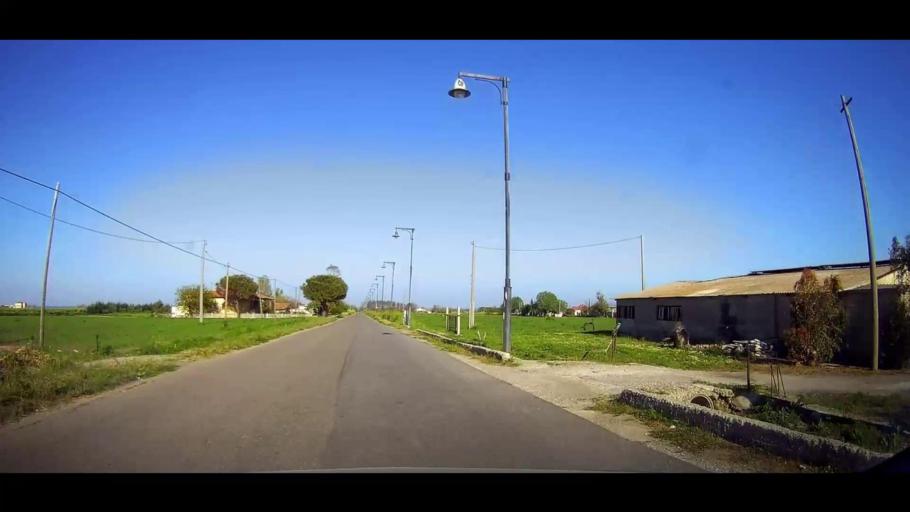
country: IT
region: Calabria
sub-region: Provincia di Crotone
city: Crotone
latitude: 39.0249
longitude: 17.1781
